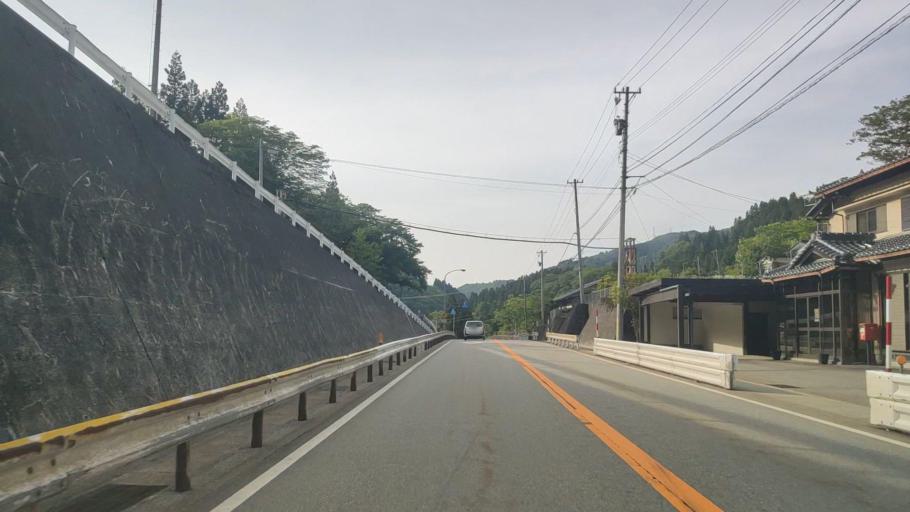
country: JP
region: Toyama
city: Yatsuomachi-higashikumisaka
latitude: 36.4572
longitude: 137.2510
